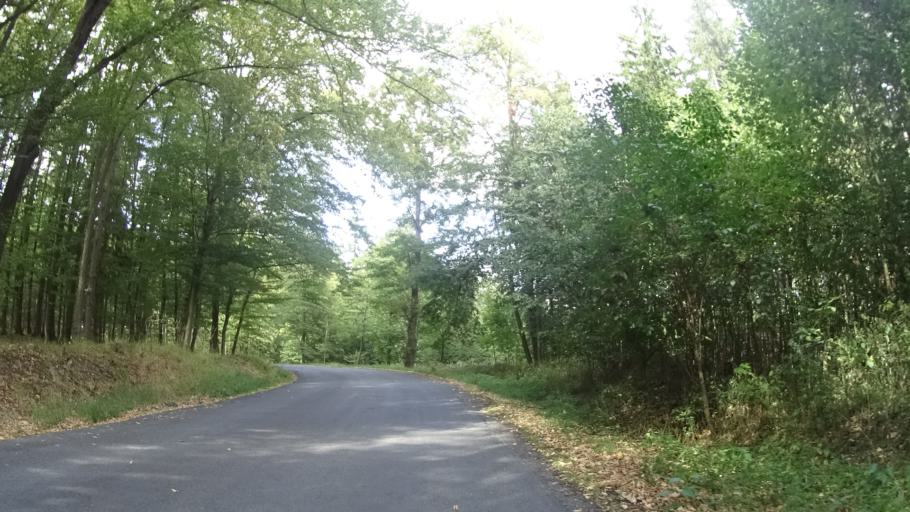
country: CZ
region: Olomoucky
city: Bila Lhota
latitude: 49.7304
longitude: 17.0096
